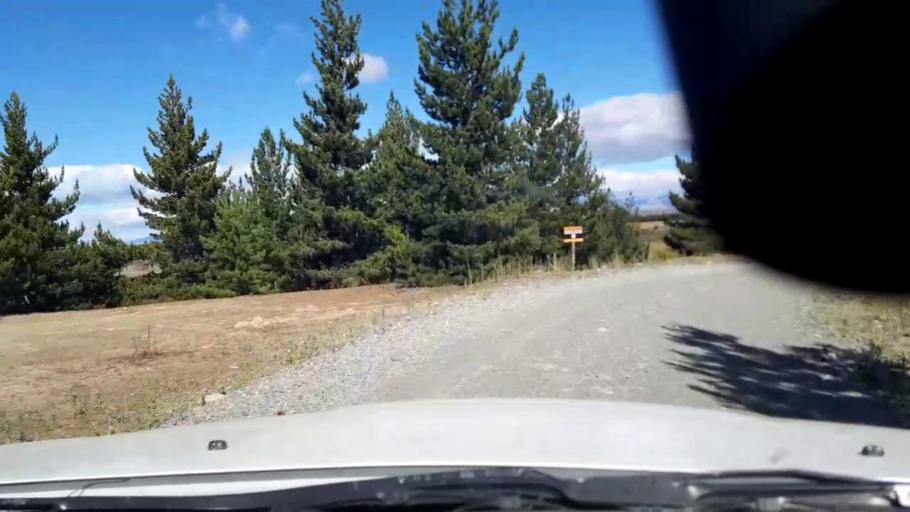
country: NZ
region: Canterbury
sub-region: Timaru District
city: Pleasant Point
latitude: -44.0151
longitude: 170.4711
